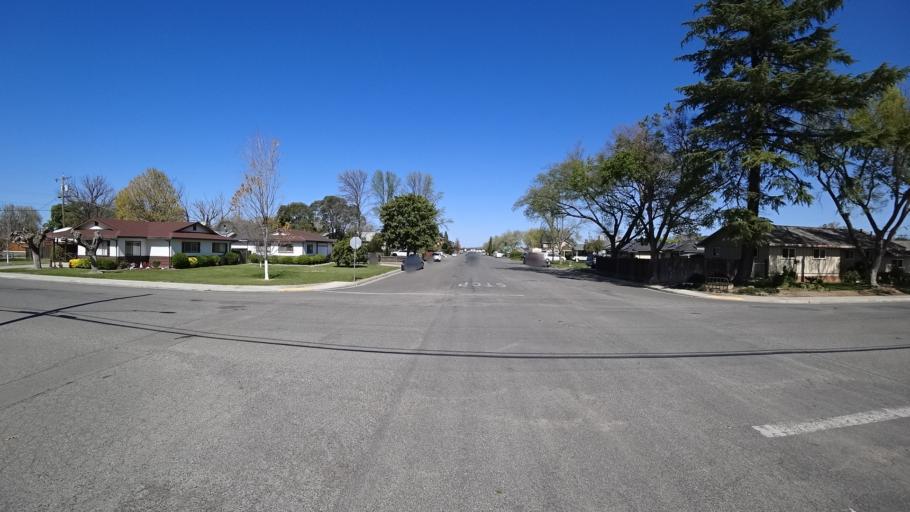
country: US
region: California
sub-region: Glenn County
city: Hamilton City
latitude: 39.7427
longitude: -122.0140
